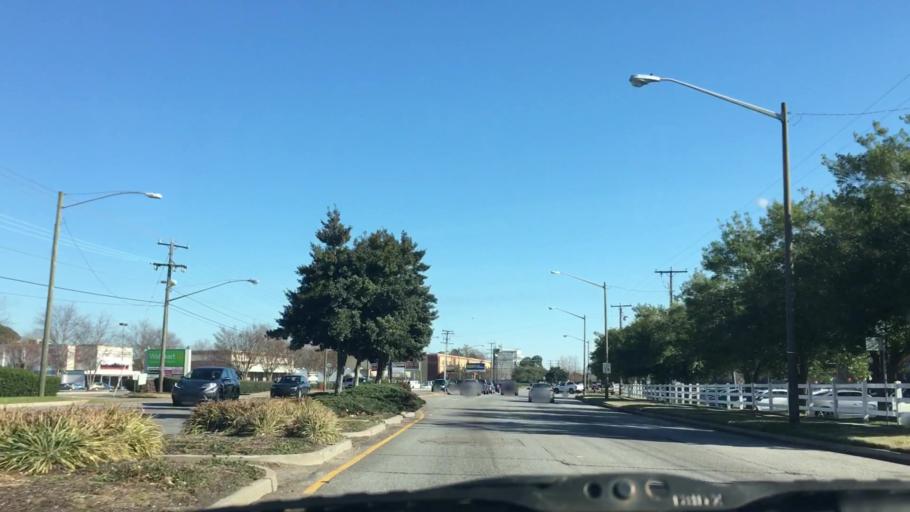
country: US
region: Virginia
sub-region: City of Norfolk
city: Norfolk
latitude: 36.9168
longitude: -76.2295
